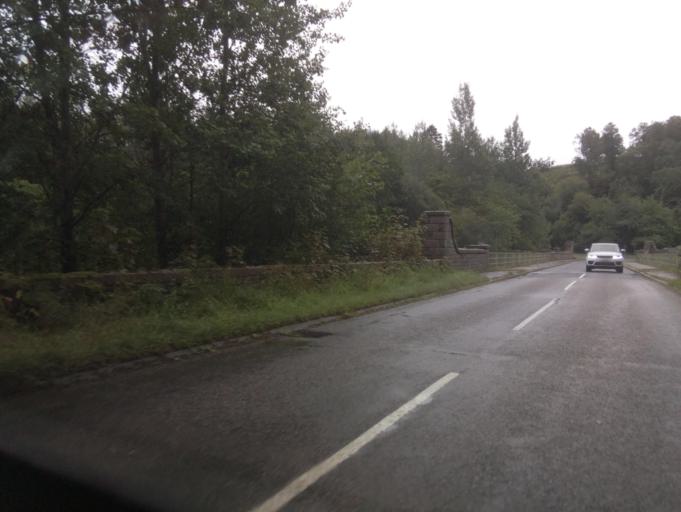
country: GB
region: Scotland
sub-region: Highland
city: Grantown on Spey
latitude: 57.2626
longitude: -3.4114
